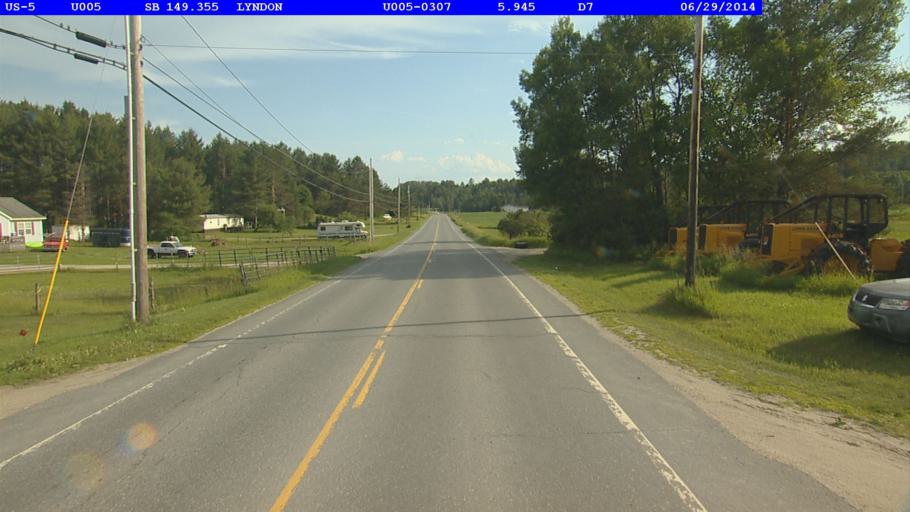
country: US
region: Vermont
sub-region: Caledonia County
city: Lyndonville
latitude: 44.5731
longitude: -71.9875
